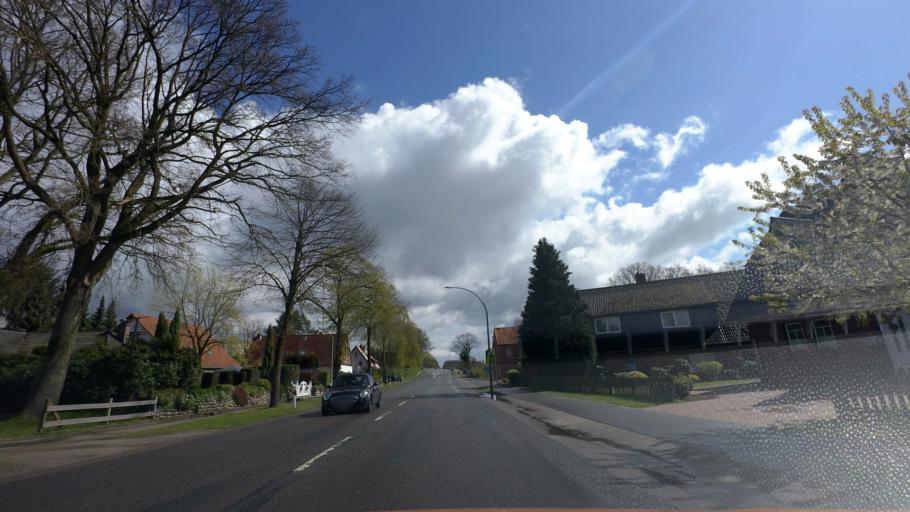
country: DE
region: Lower Saxony
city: Reessum
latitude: 53.1084
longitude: 9.1946
